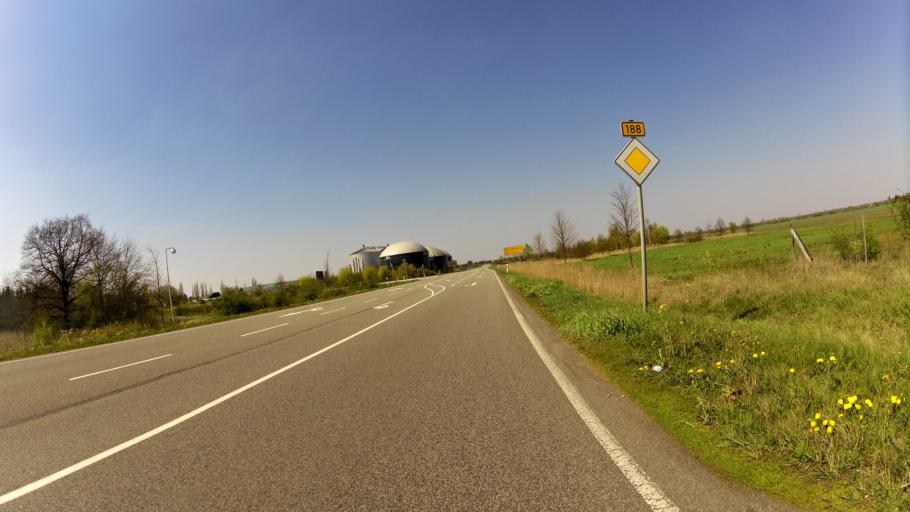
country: DE
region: Saxony-Anhalt
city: Oebisfelde
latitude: 52.4436
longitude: 10.9947
